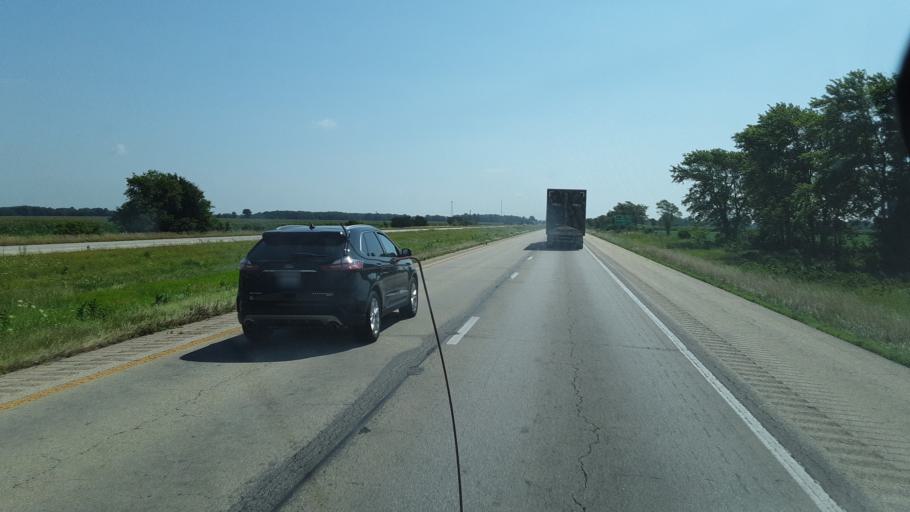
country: US
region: Illinois
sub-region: Effingham County
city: Teutopolis
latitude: 39.1651
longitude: -88.4033
